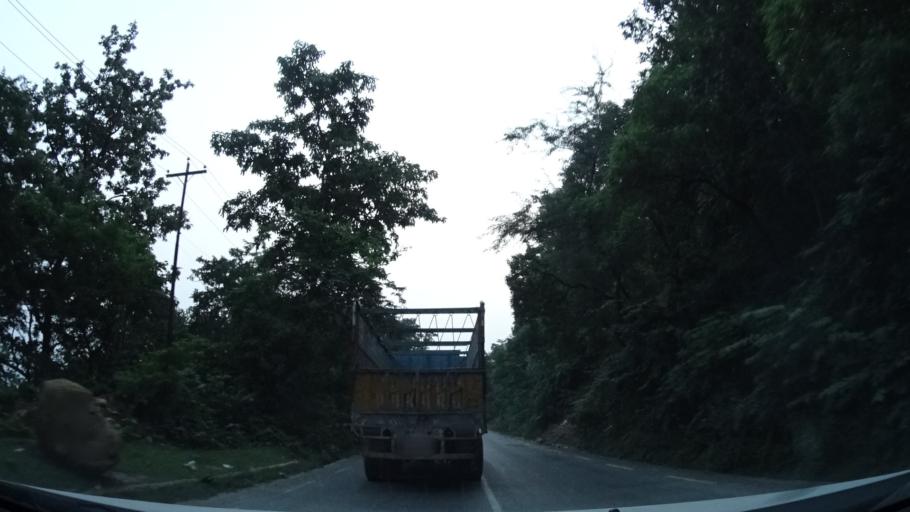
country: IN
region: Uttar Pradesh
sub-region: Maharajganj
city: Nichlaul
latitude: 27.5506
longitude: 83.8297
